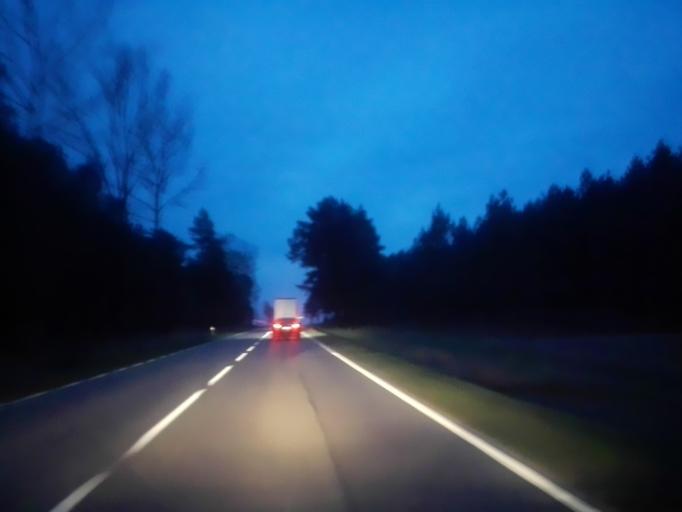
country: PL
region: Podlasie
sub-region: Powiat lomzynski
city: Sniadowo
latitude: 53.0909
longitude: 22.0222
